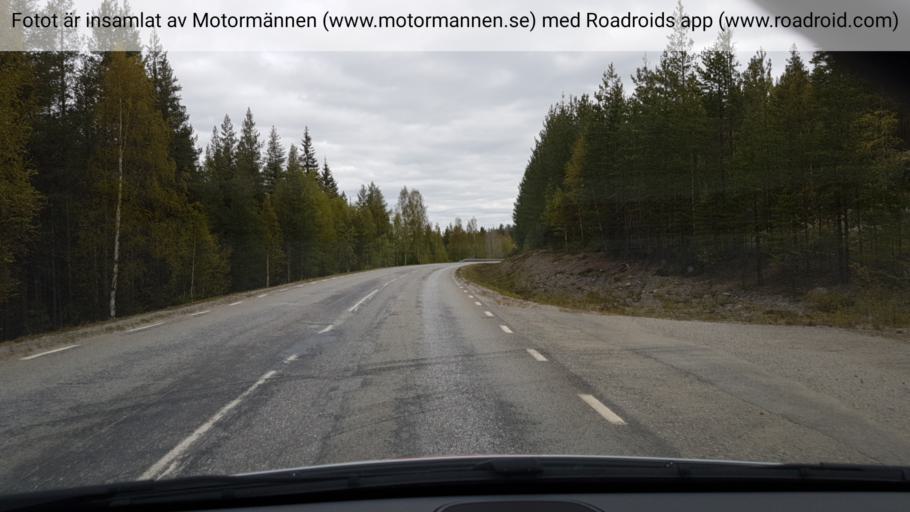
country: SE
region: Vaesterbotten
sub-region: Lycksele Kommun
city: Lycksele
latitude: 64.8642
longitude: 18.7211
